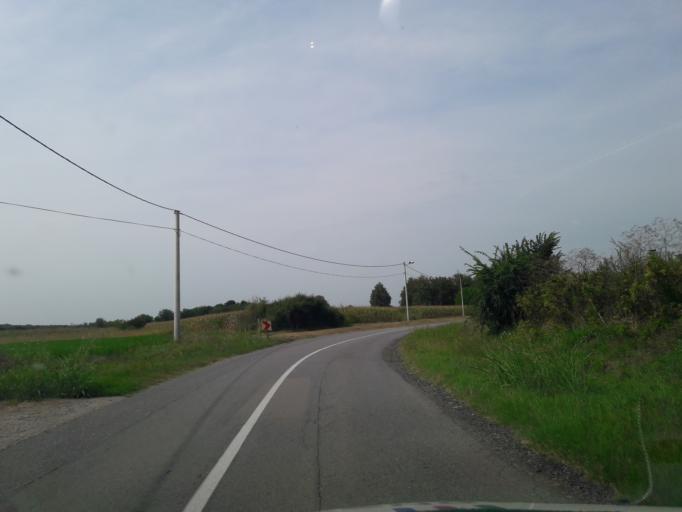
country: HR
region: Vukovarsko-Srijemska
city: Nustar
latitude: 45.3646
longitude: 18.8549
